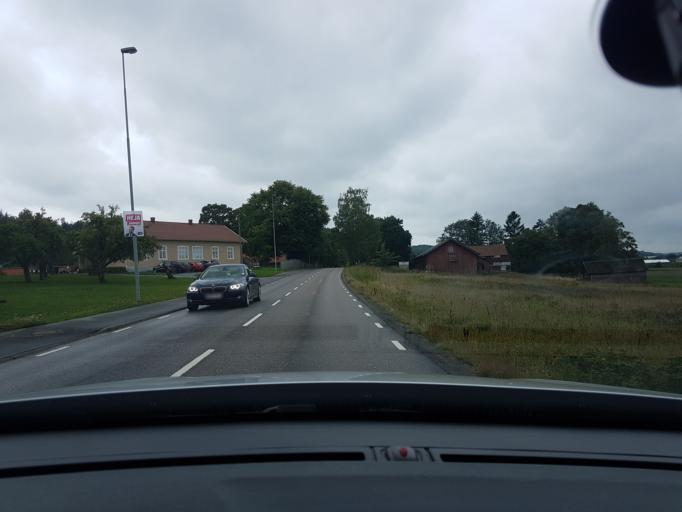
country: SE
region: Vaestra Goetaland
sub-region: Ale Kommun
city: Skepplanda
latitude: 57.9824
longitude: 12.2032
